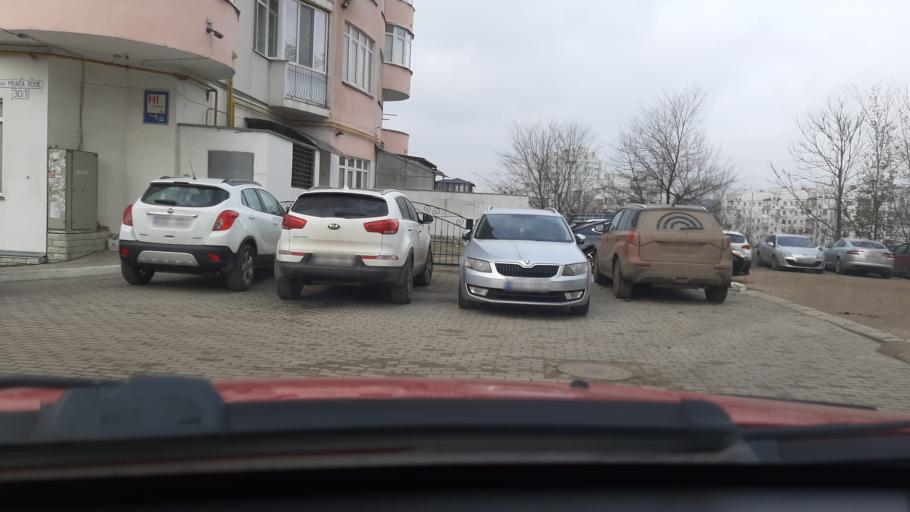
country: MD
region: Chisinau
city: Chisinau
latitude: 47.0371
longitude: 28.8371
